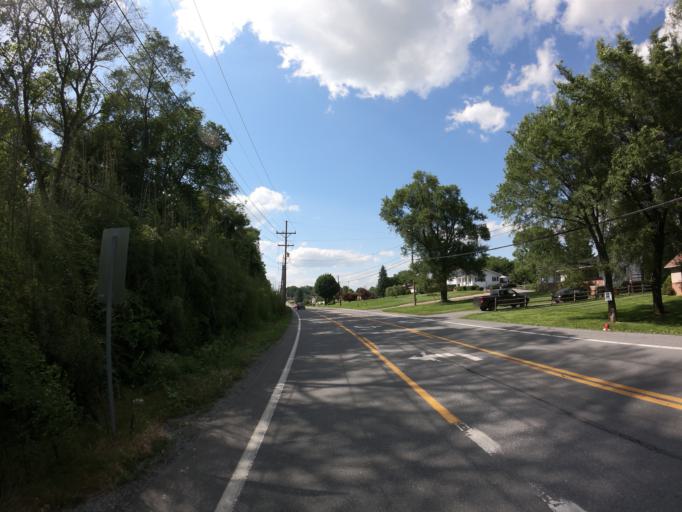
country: US
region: West Virginia
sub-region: Berkeley County
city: Martinsburg
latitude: 39.4075
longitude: -77.9125
